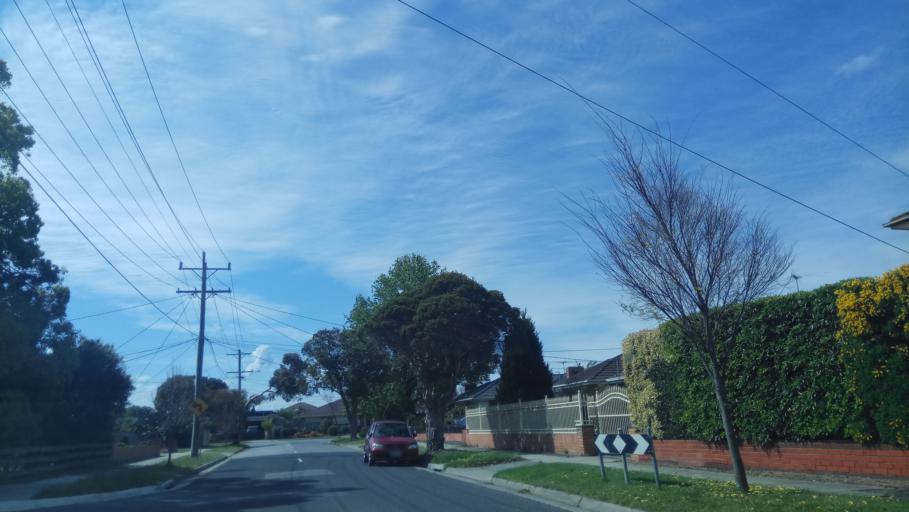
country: AU
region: Victoria
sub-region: Greater Dandenong
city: Springvale South
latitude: -37.9610
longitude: 145.1464
